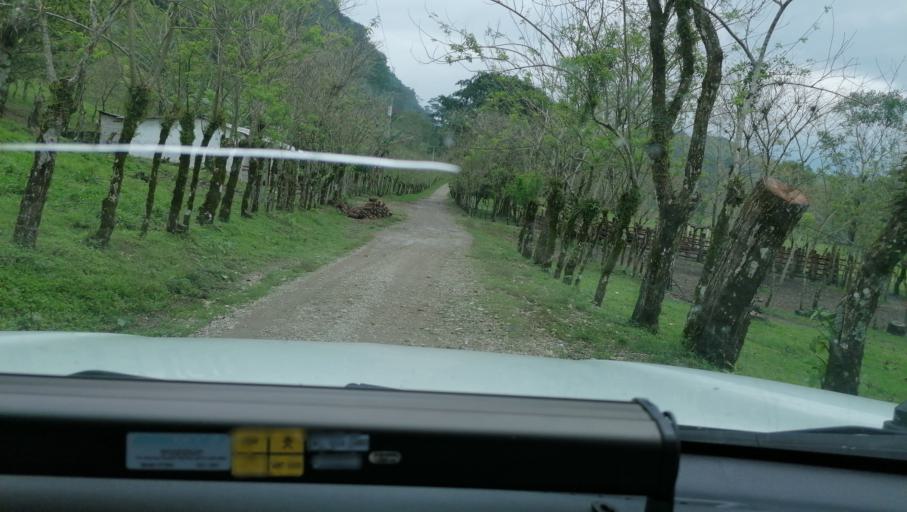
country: MX
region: Chiapas
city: Ixtacomitan
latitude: 17.3511
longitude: -93.1560
